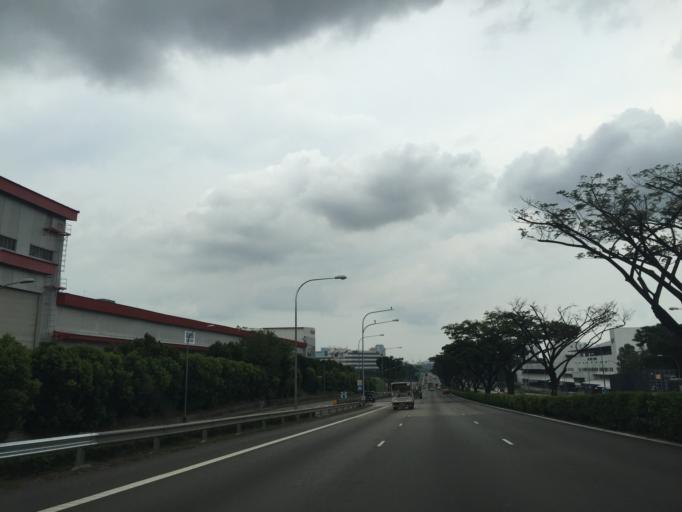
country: SG
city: Singapore
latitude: 1.3223
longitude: 103.7136
